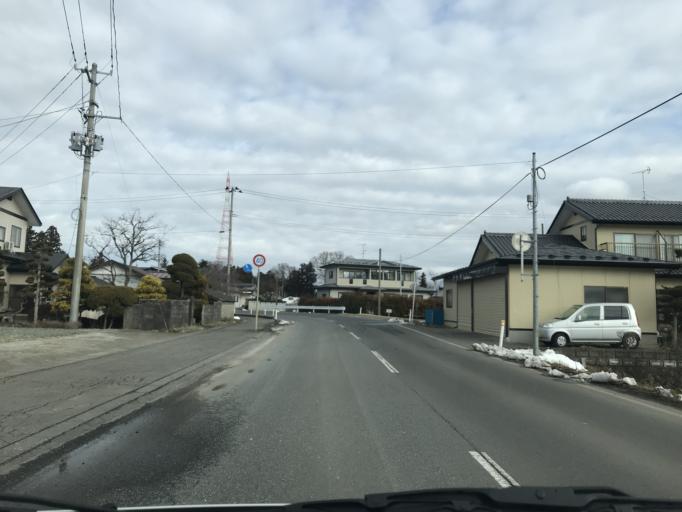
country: JP
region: Iwate
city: Mizusawa
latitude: 39.0713
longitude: 141.1635
